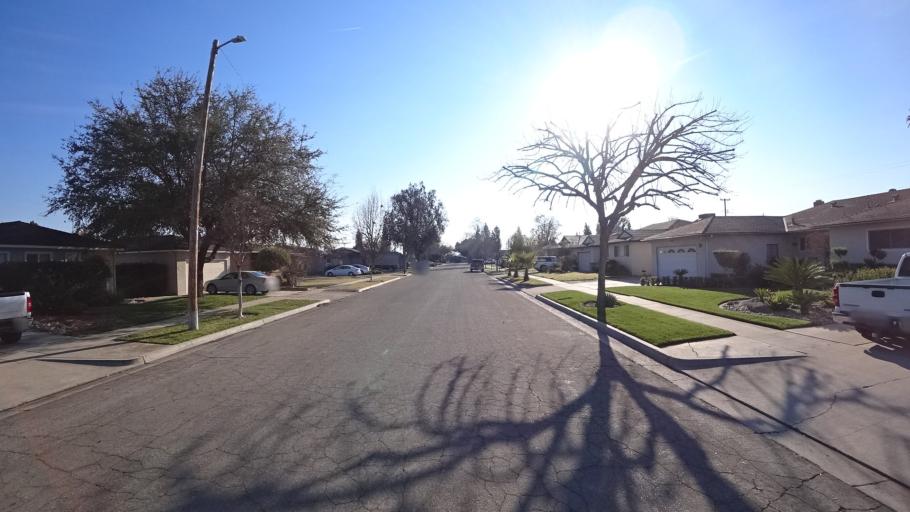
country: US
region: California
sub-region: Fresno County
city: Fresno
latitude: 36.8174
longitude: -119.7749
